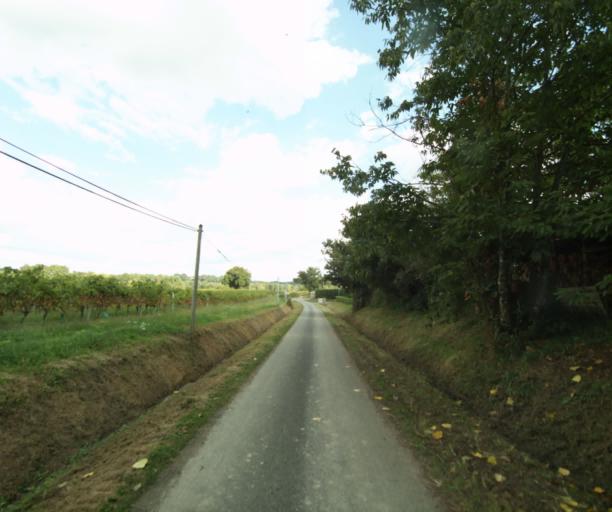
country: FR
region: Midi-Pyrenees
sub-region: Departement du Gers
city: Cazaubon
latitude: 43.8978
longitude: -0.0509
